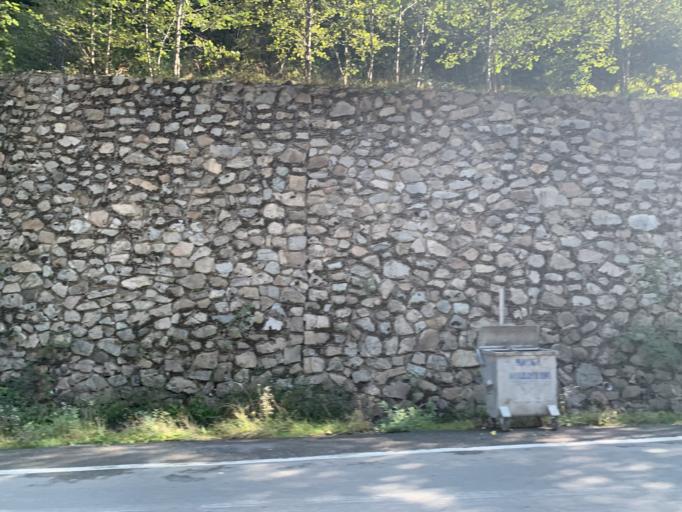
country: TR
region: Trabzon
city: Macka
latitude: 40.7036
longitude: 39.6511
